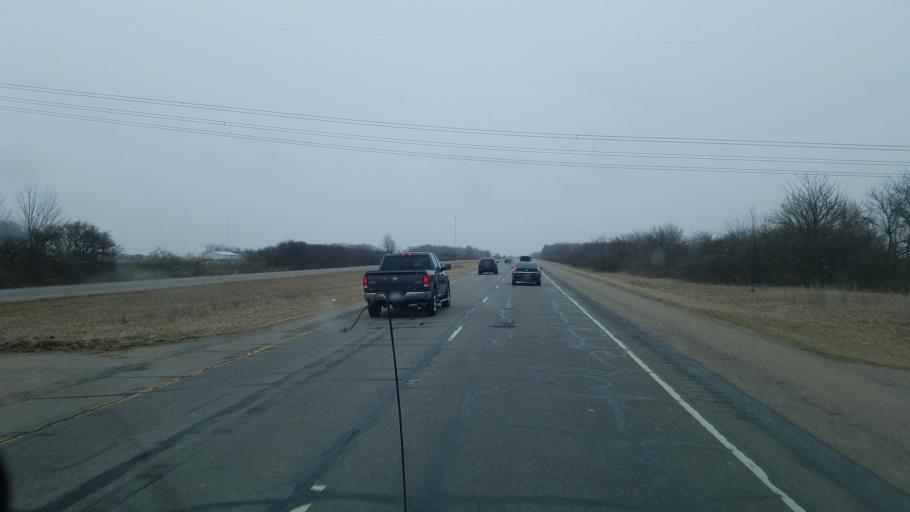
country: US
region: Indiana
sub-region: Miami County
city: Peru
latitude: 40.8078
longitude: -85.9807
